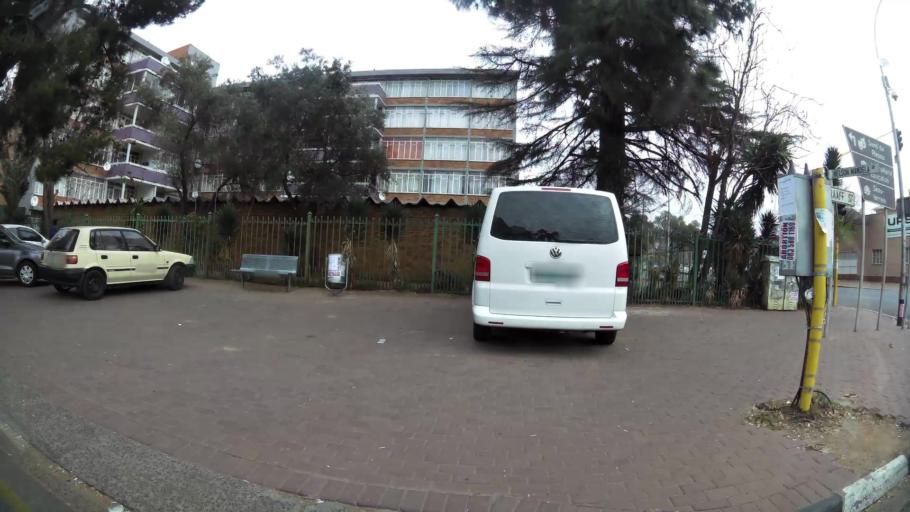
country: ZA
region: Orange Free State
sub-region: Mangaung Metropolitan Municipality
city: Bloemfontein
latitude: -29.1130
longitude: 26.2147
